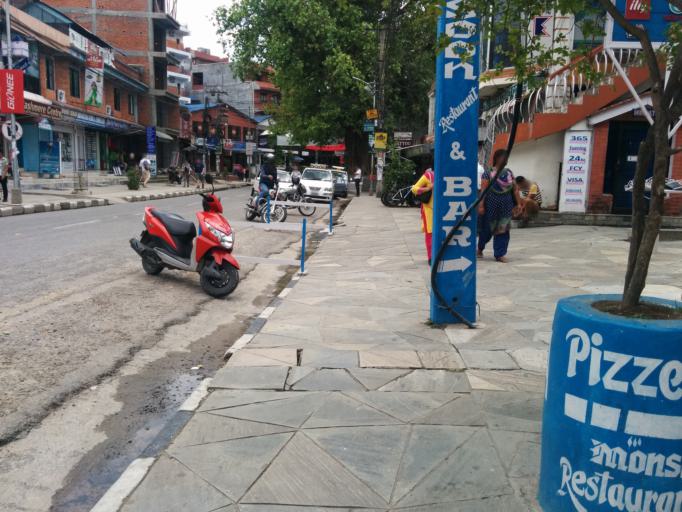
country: NP
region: Western Region
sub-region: Gandaki Zone
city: Pokhara
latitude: 28.2089
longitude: 83.9572
